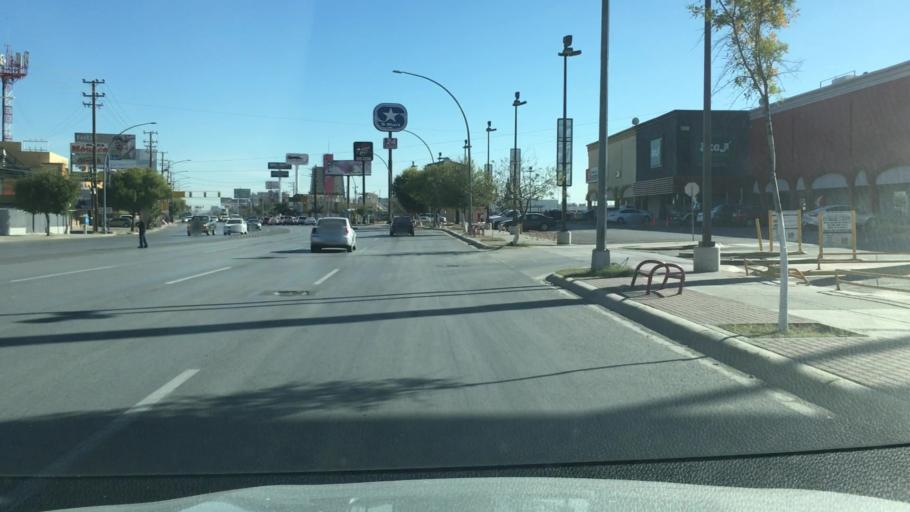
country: MX
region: Chihuahua
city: Ciudad Juarez
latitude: 31.7368
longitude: -106.4476
